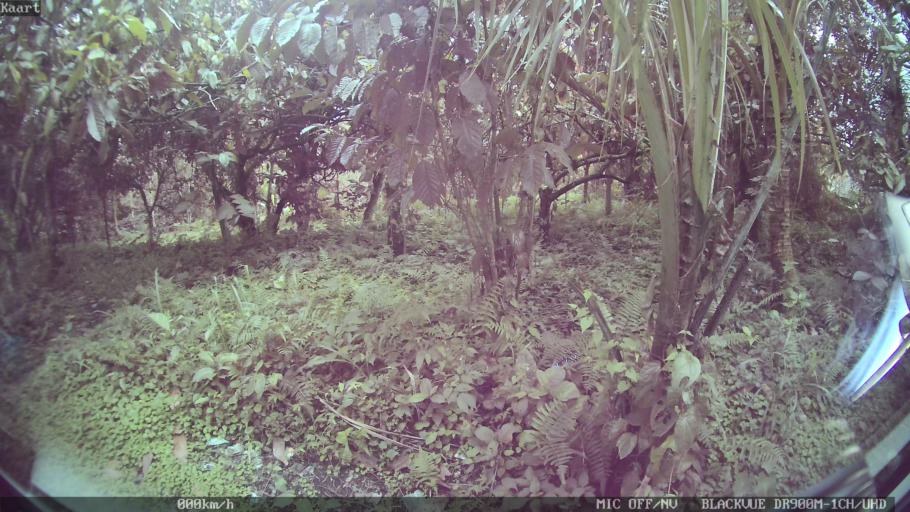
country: ID
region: Bali
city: Peneng
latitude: -8.3572
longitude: 115.2055
